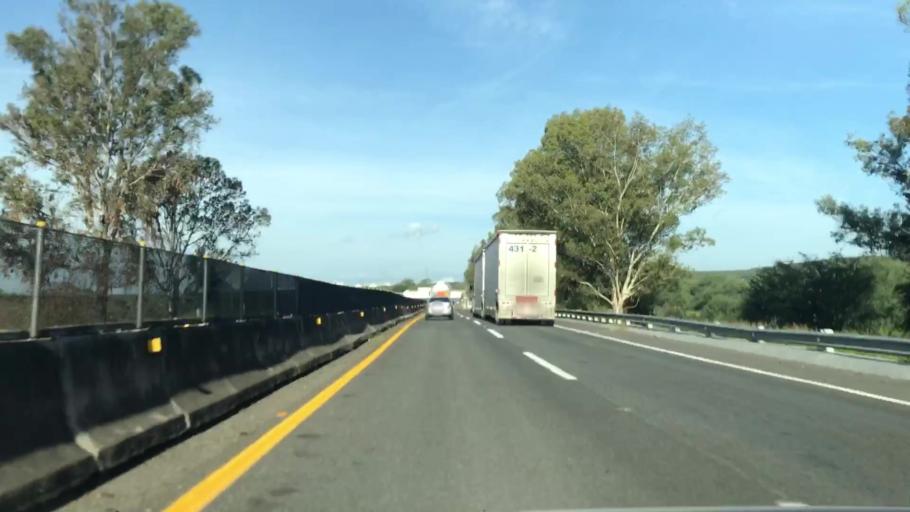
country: MX
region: Jalisco
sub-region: Lagos de Moreno
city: Cristeros [Fraccionamiento]
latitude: 21.3179
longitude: -102.0508
